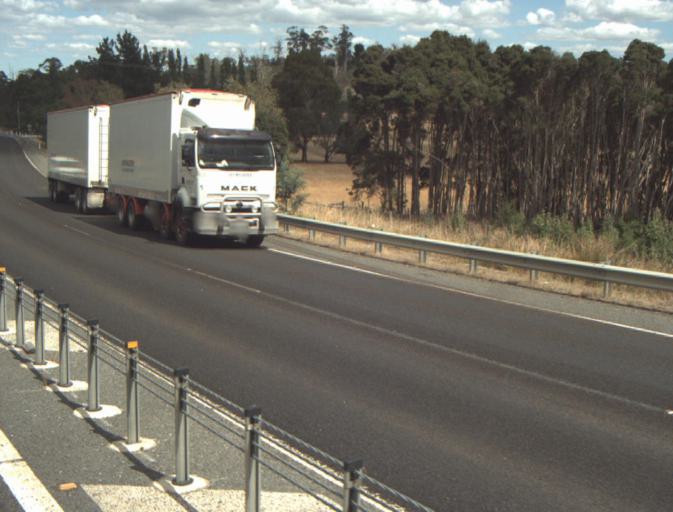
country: AU
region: Tasmania
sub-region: Launceston
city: Mayfield
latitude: -41.2925
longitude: 147.0476
